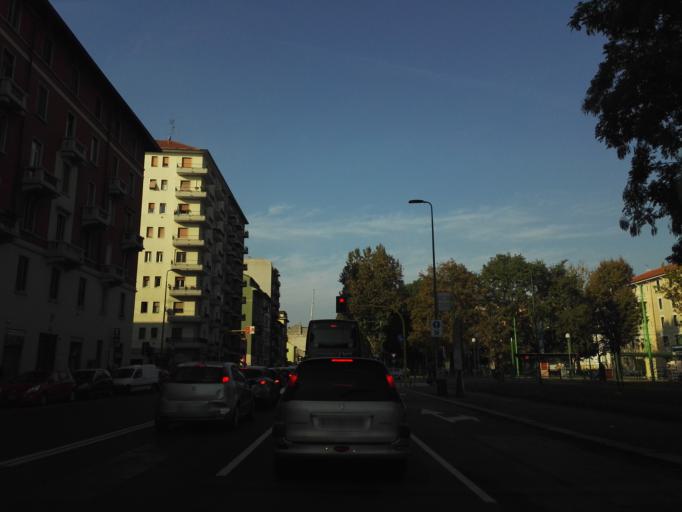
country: IT
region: Lombardy
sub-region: Citta metropolitana di Milano
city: Milano
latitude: 45.4374
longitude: 9.1843
